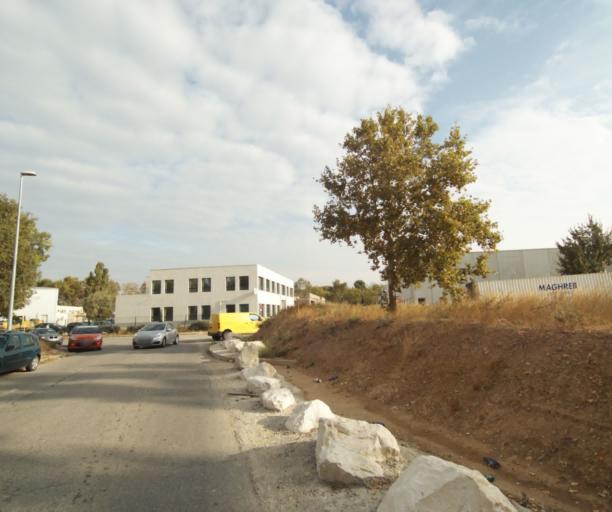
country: FR
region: Provence-Alpes-Cote d'Azur
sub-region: Departement des Bouches-du-Rhone
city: Saint-Victoret
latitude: 43.4216
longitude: 5.2598
